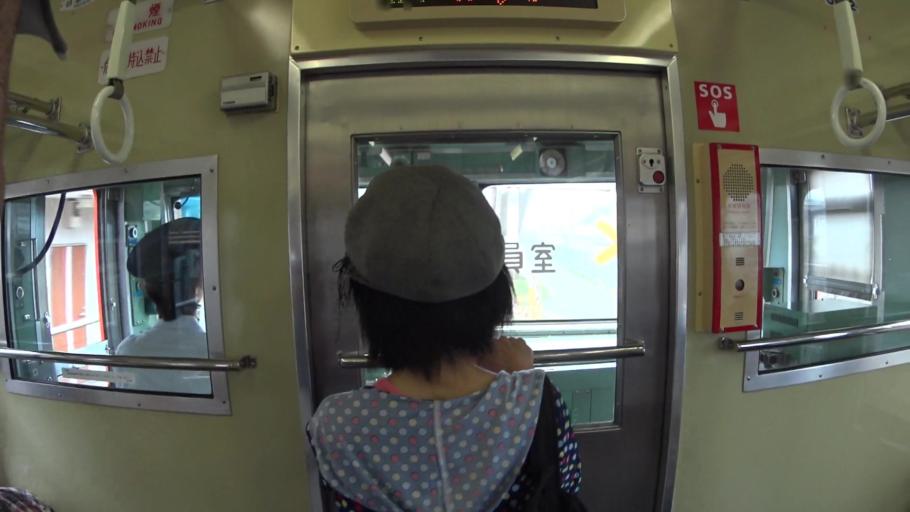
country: JP
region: Chiba
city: Nagareyama
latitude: 35.8194
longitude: 139.9188
